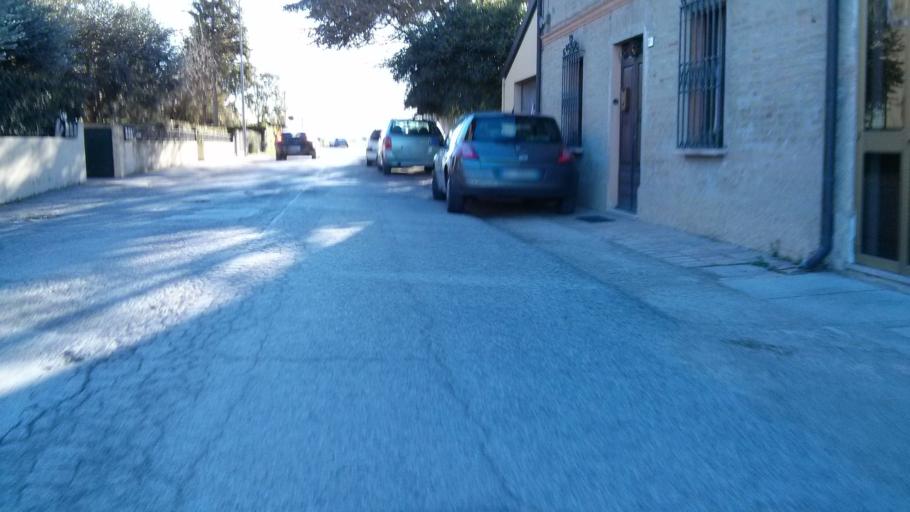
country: IT
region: The Marches
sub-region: Provincia di Pesaro e Urbino
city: Fano
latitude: 43.8302
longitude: 13.0235
